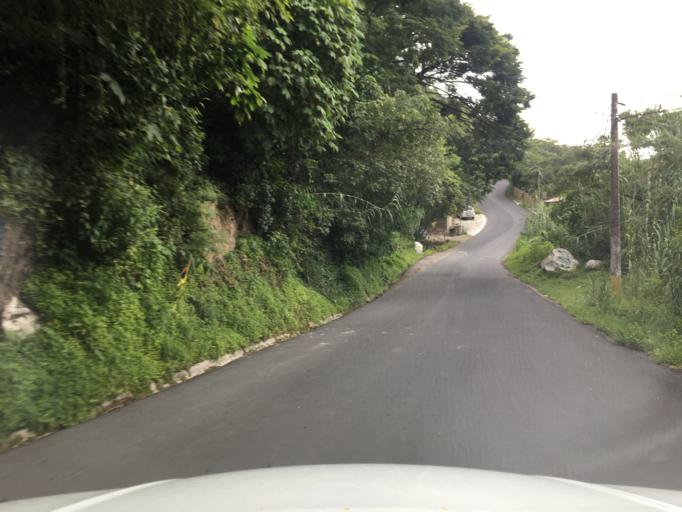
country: GT
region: Solola
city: Panajachel
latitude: 14.7323
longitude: -91.1427
